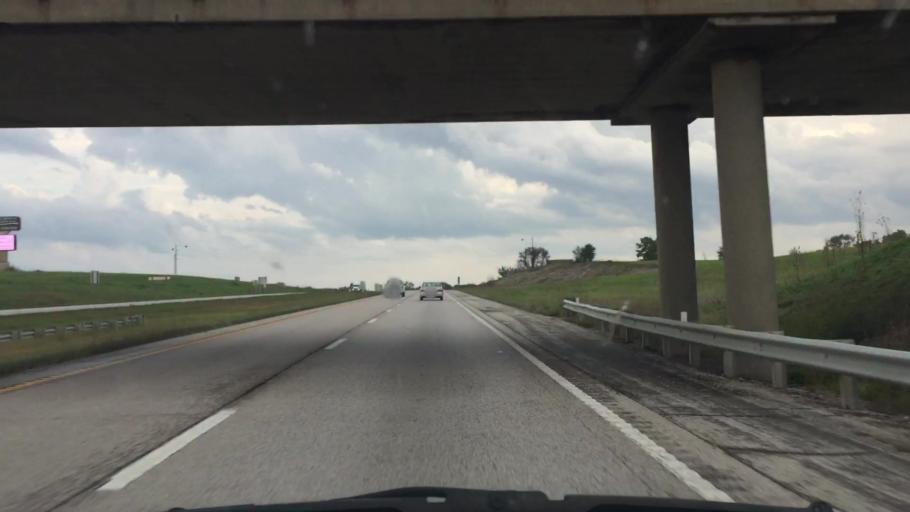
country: US
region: Missouri
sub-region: Clinton County
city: Cameron
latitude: 39.7316
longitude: -94.2207
